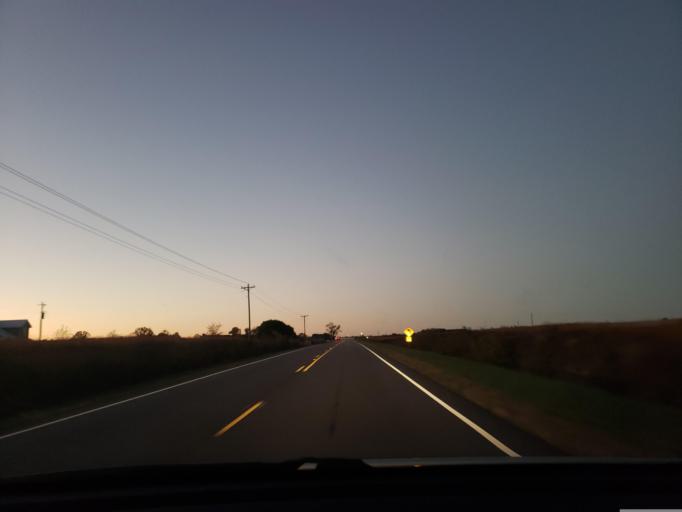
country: US
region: North Carolina
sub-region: Duplin County
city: Kenansville
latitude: 34.8957
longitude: -77.9098
